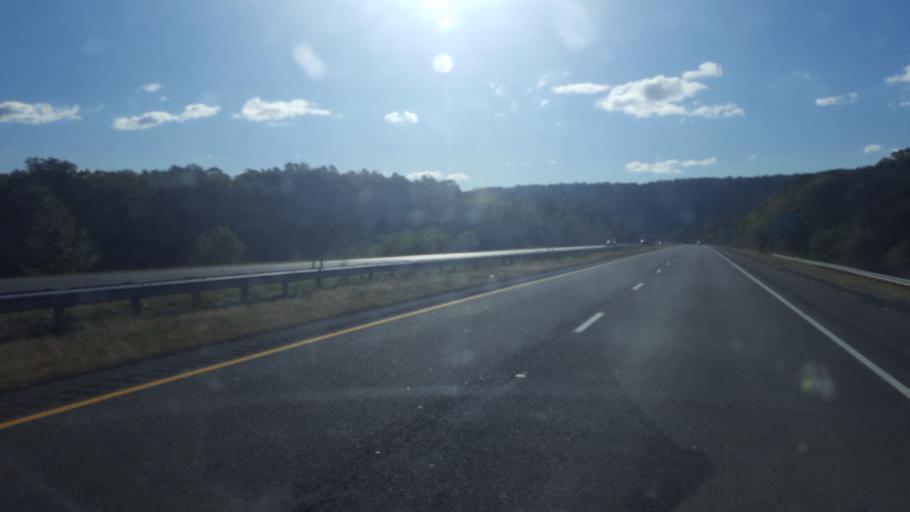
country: US
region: Maryland
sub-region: Washington County
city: Hancock
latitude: 39.7041
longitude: -78.2580
